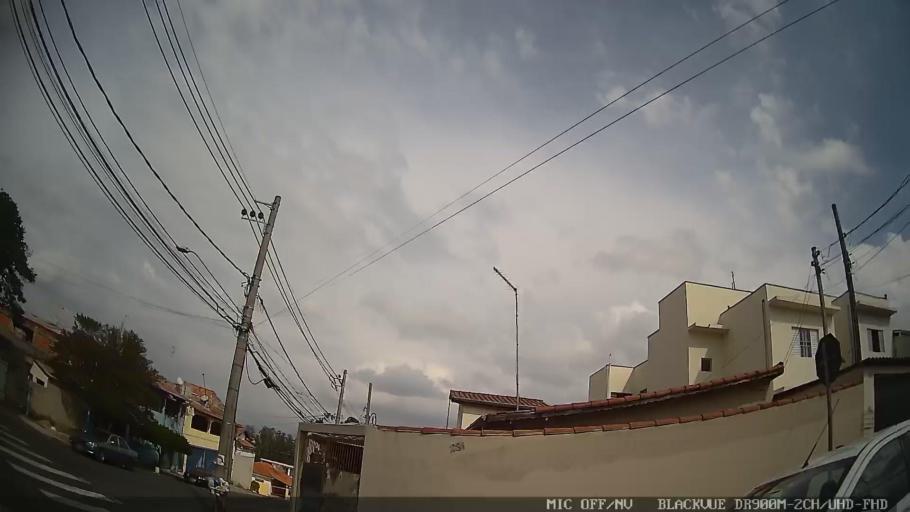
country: BR
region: Sao Paulo
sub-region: Indaiatuba
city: Indaiatuba
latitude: -23.1288
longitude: -47.2374
